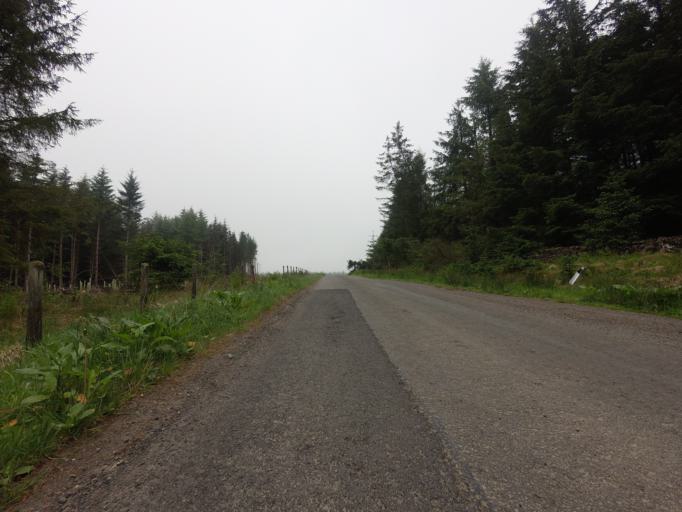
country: GB
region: Scotland
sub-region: Fife
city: Townhill
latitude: 56.1456
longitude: -3.4512
